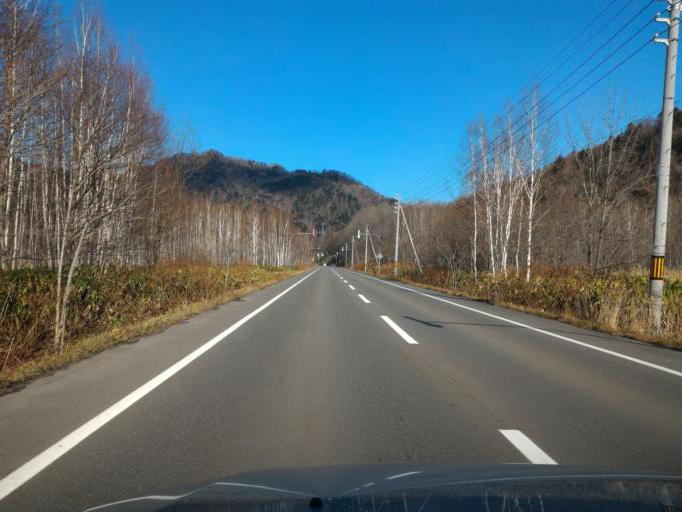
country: JP
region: Hokkaido
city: Ashibetsu
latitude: 43.3627
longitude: 142.1634
